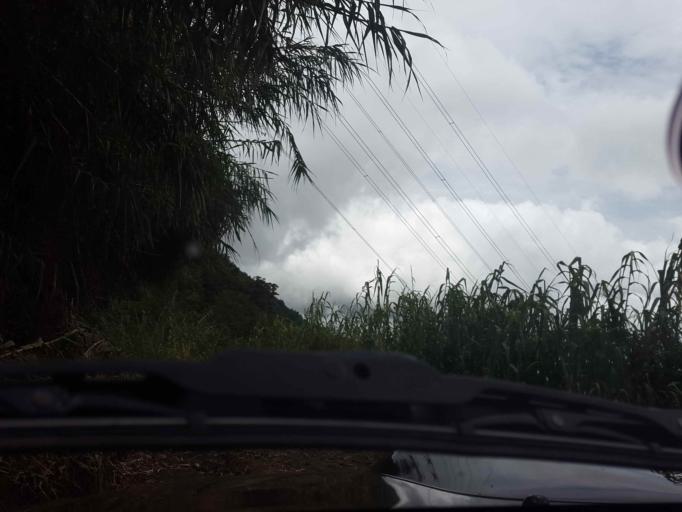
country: ID
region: Central Java
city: Wonosobo
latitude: -7.2400
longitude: 109.9059
